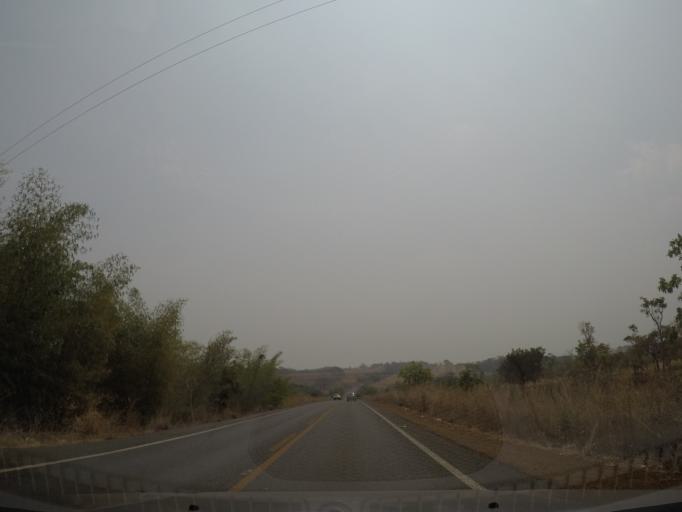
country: BR
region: Goias
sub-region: Pirenopolis
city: Pirenopolis
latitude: -15.8903
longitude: -48.8935
